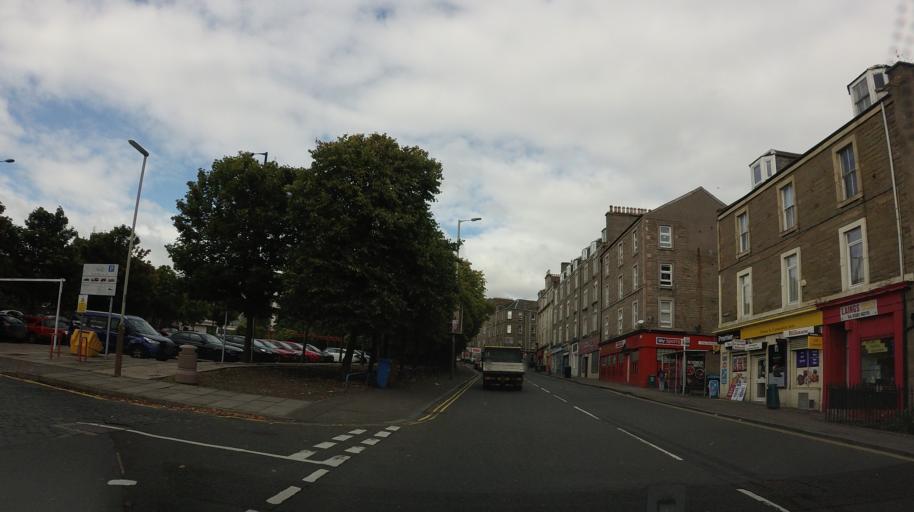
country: GB
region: Scotland
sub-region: Dundee City
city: Dundee
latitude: 56.4672
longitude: -2.9585
